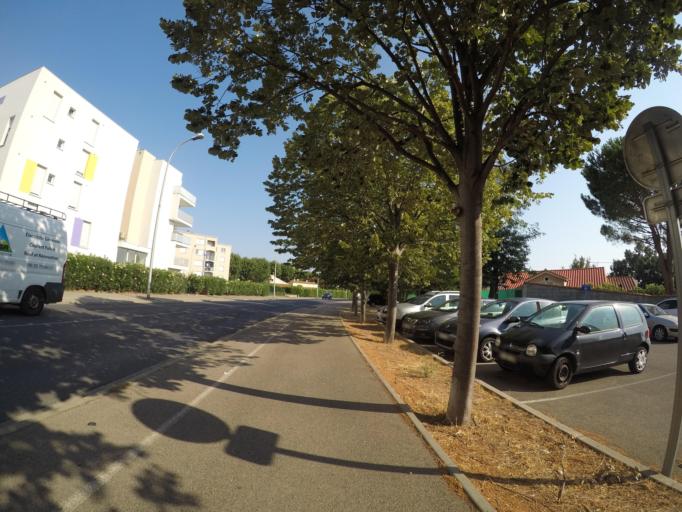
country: FR
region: Languedoc-Roussillon
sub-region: Departement des Pyrenees-Orientales
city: Thuir
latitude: 42.6305
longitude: 2.7602
